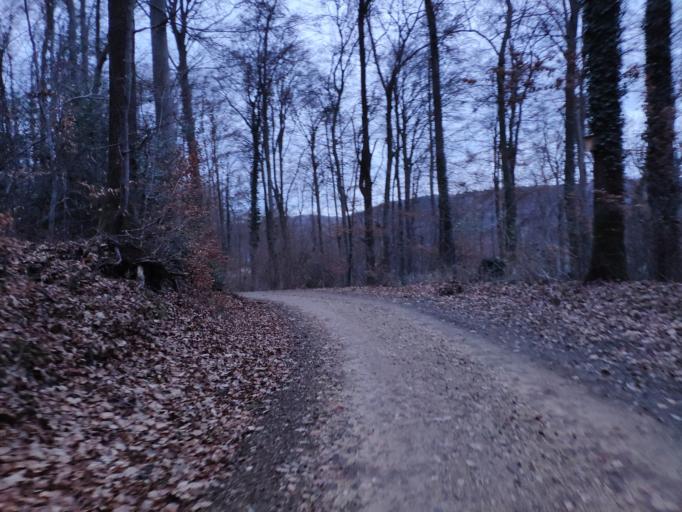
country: DE
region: Baden-Wuerttemberg
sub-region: Freiburg Region
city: Inzlingen
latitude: 47.5931
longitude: 7.6759
